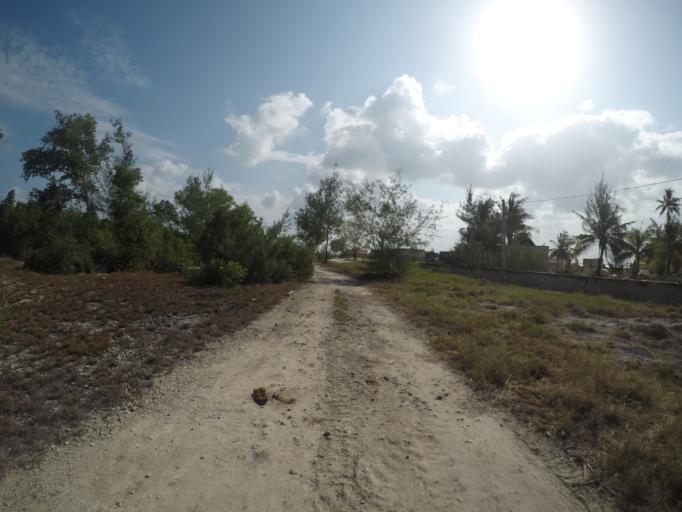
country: TZ
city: Kiwengwa
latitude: -6.1435
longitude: 39.4904
